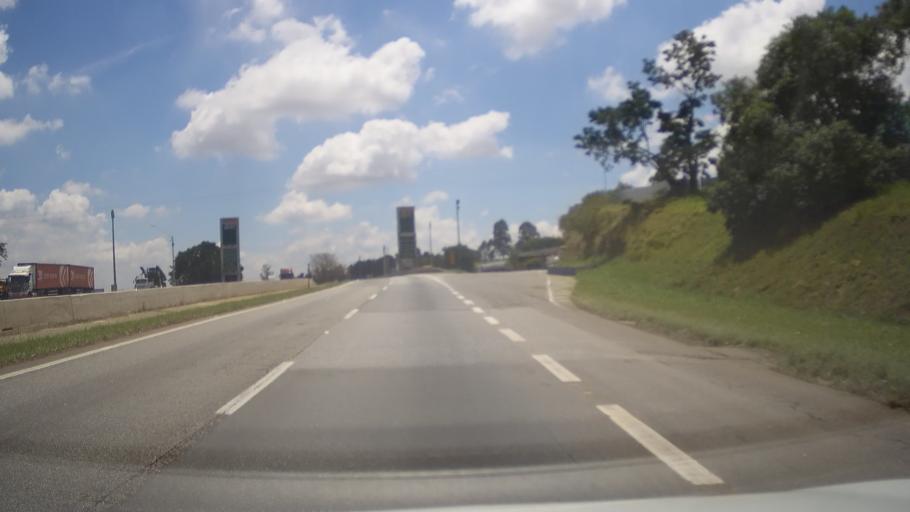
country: BR
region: Minas Gerais
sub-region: Sao Goncalo Do Sapucai
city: Sao Goncalo do Sapucai
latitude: -21.9468
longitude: -45.6211
